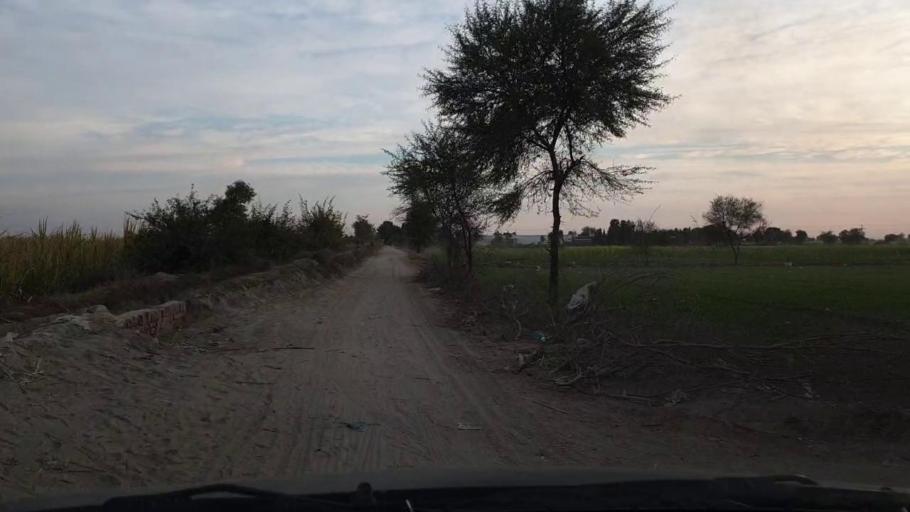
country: PK
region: Sindh
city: Khadro
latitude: 26.1280
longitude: 68.7778
